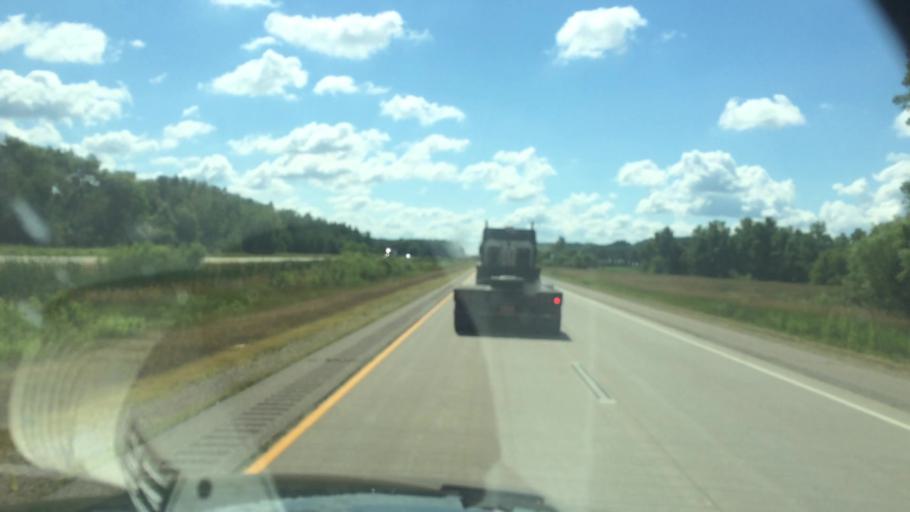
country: US
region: Wisconsin
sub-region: Waupaca County
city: King
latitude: 44.3970
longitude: -89.2093
